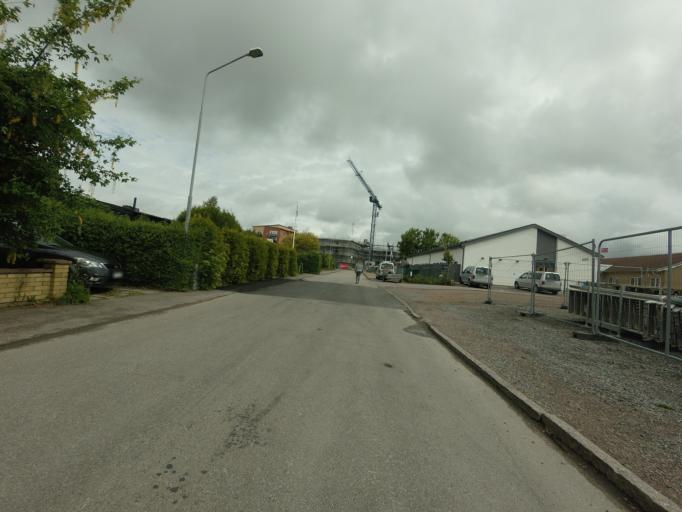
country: SE
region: Skane
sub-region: Hoganas Kommun
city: Hoganas
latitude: 56.1962
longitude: 12.5756
